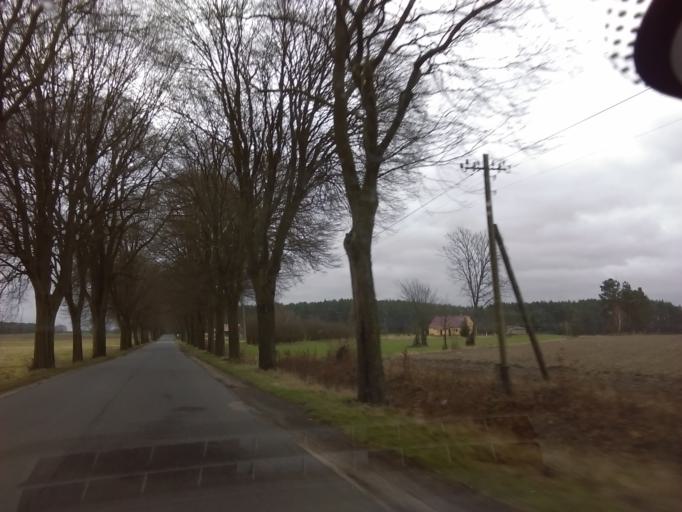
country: PL
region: Greater Poland Voivodeship
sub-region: Powiat zlotowski
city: Lipka
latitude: 53.4644
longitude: 17.3152
